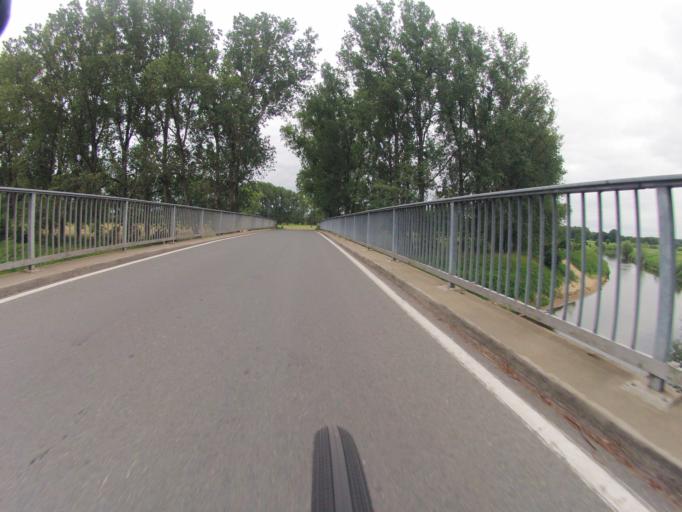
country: DE
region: North Rhine-Westphalia
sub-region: Regierungsbezirk Munster
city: Saerbeck
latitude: 52.1677
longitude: 7.6117
